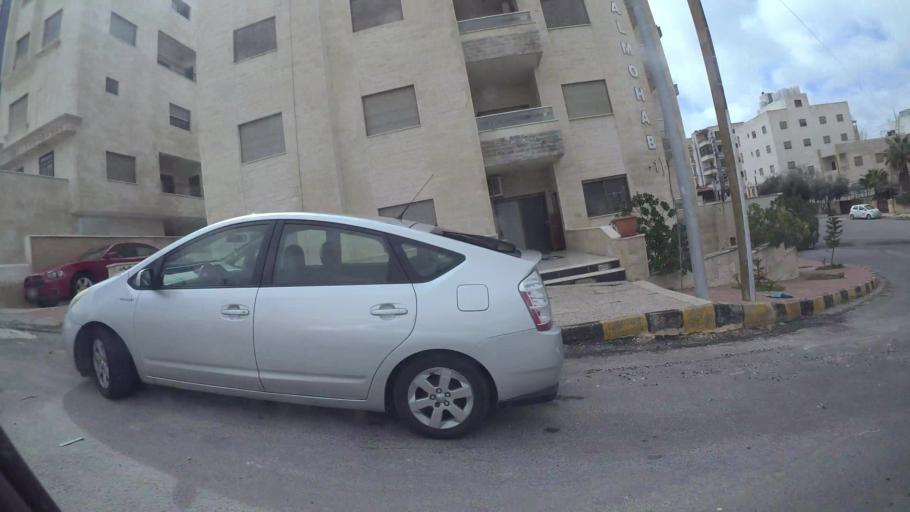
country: JO
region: Amman
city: Al Jubayhah
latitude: 32.0650
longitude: 35.8747
